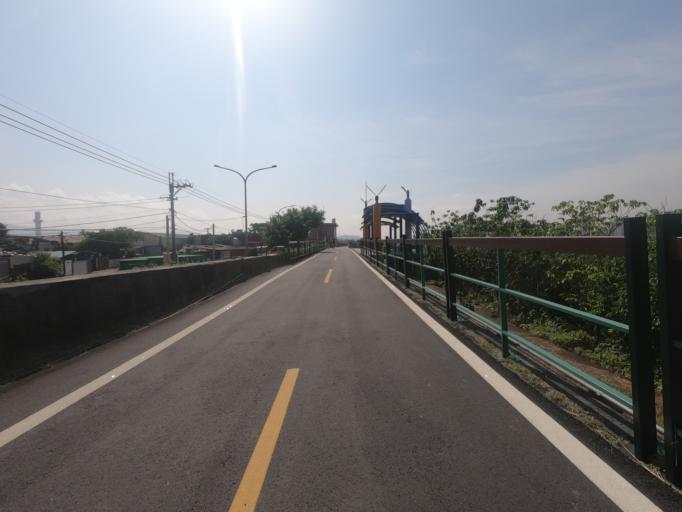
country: TW
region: Taipei
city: Taipei
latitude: 25.1030
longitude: 121.4829
